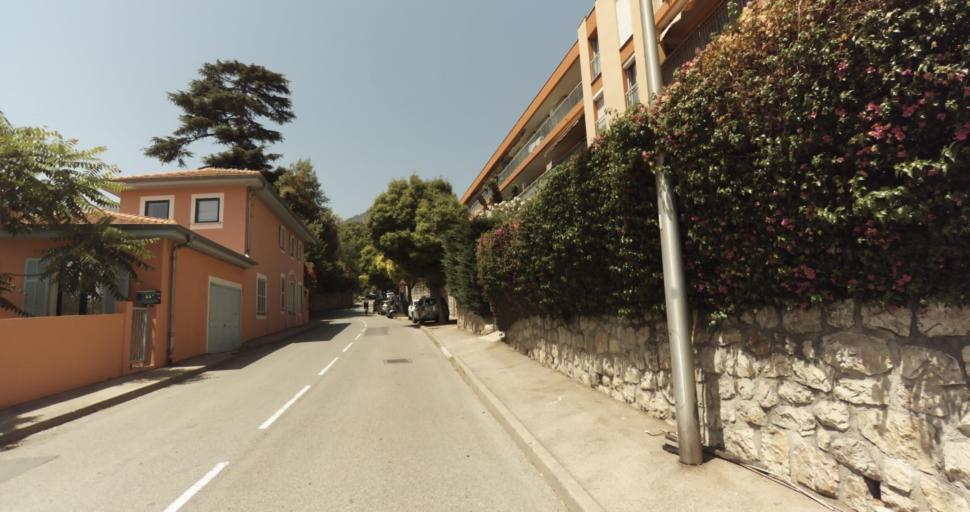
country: FR
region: Provence-Alpes-Cote d'Azur
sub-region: Departement des Alpes-Maritimes
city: Roquebrune-Cap-Martin
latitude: 43.7767
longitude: 7.4731
